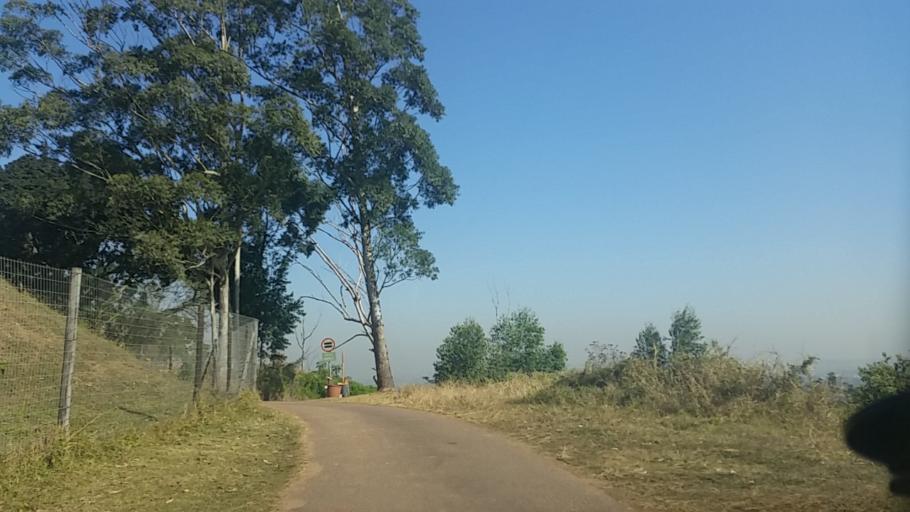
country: ZA
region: KwaZulu-Natal
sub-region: eThekwini Metropolitan Municipality
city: Berea
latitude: -29.8405
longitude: 30.9002
